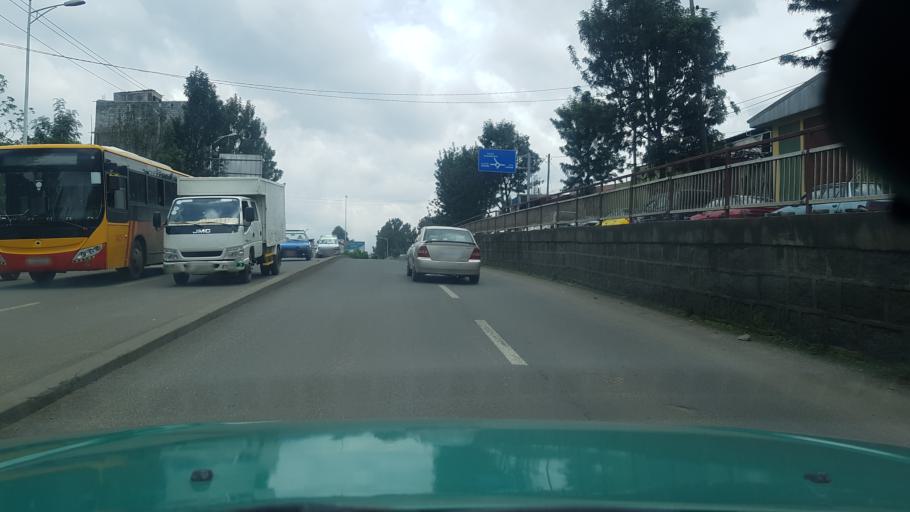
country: ET
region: Adis Abeba
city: Addis Ababa
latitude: 9.0234
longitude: 38.7779
